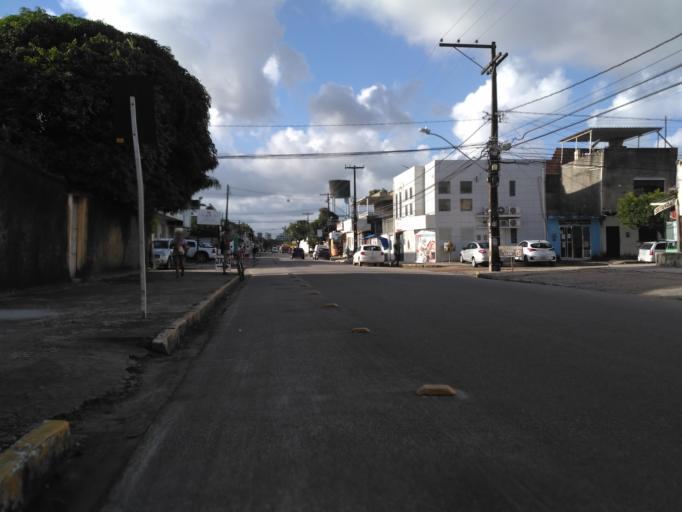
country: BR
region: Pernambuco
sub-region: Recife
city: Recife
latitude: -8.0604
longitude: -34.9425
